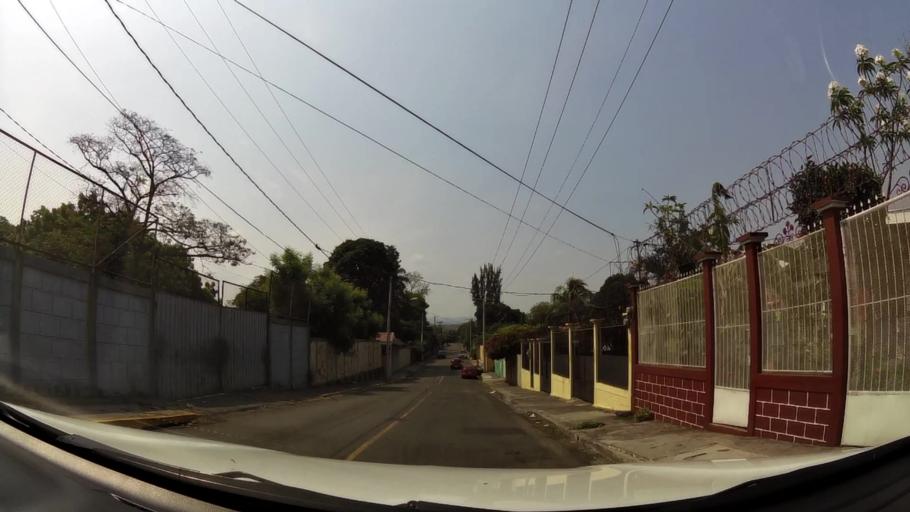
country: NI
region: Managua
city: Ciudad Sandino
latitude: 12.1321
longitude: -86.3146
